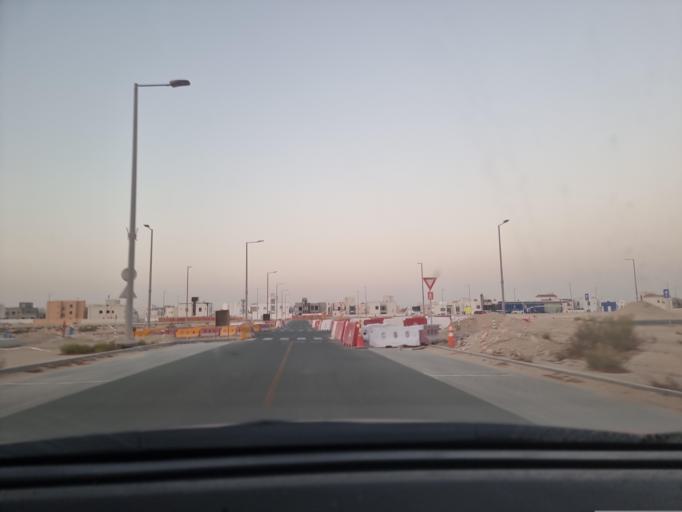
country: AE
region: Abu Dhabi
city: Abu Dhabi
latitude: 24.3704
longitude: 54.7422
